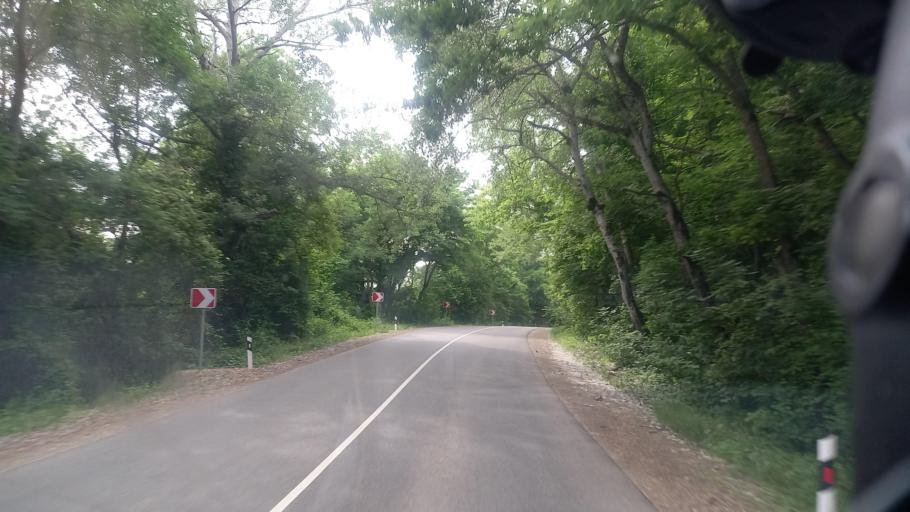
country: RU
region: Krasnodarskiy
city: Goryachiy Klyuch
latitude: 44.5998
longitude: 39.0471
